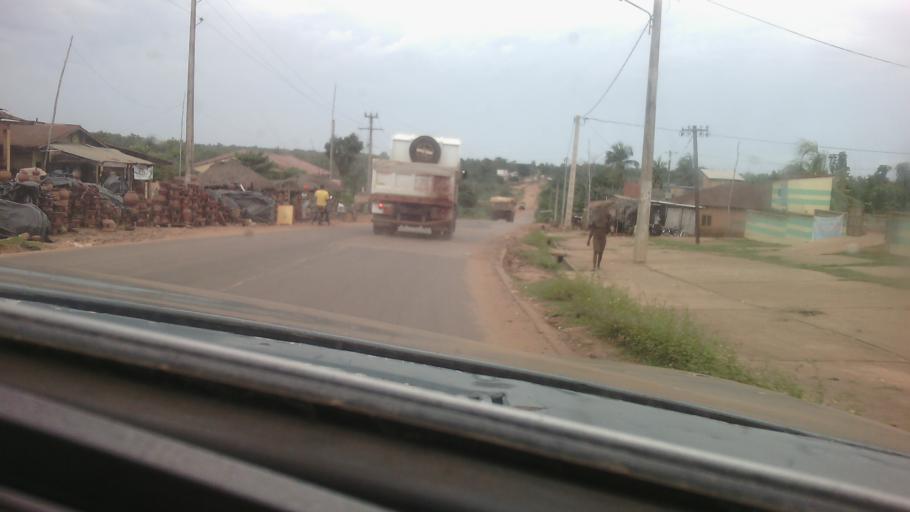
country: BJ
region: Mono
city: Come
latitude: 6.5088
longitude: 1.8294
